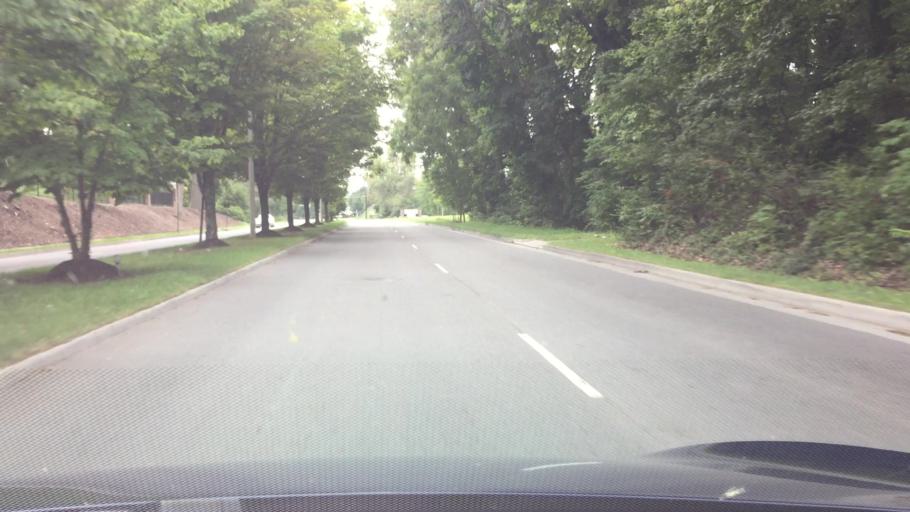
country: US
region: Virginia
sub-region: City of Radford
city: Radford
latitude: 37.1321
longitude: -80.5498
